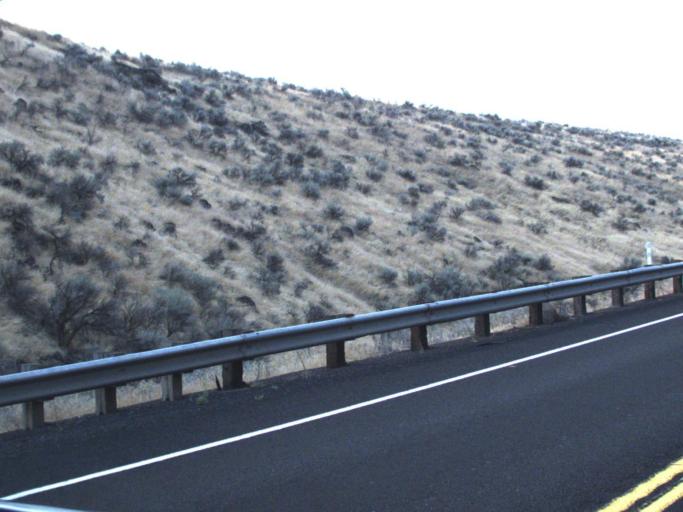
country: US
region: Washington
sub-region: Yakima County
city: Toppenish
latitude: 46.2901
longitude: -120.3613
